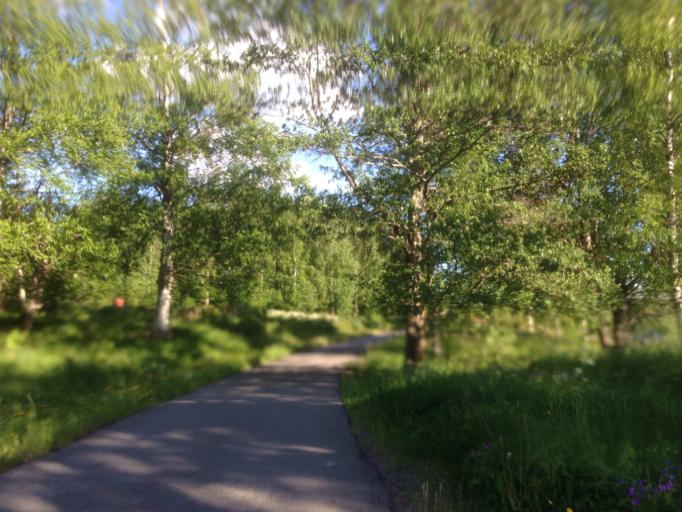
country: SE
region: Dalarna
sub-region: Ludvika Kommun
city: Ludvika
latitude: 60.1115
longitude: 15.2072
